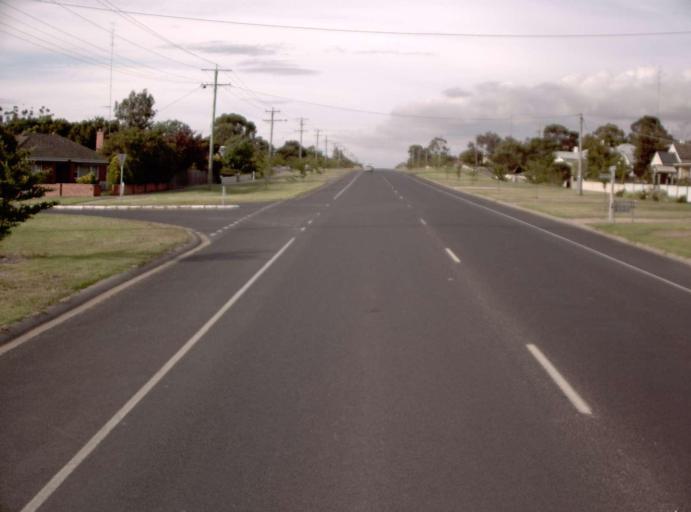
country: AU
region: Victoria
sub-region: Wellington
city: Sale
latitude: -37.9702
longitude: 146.9842
